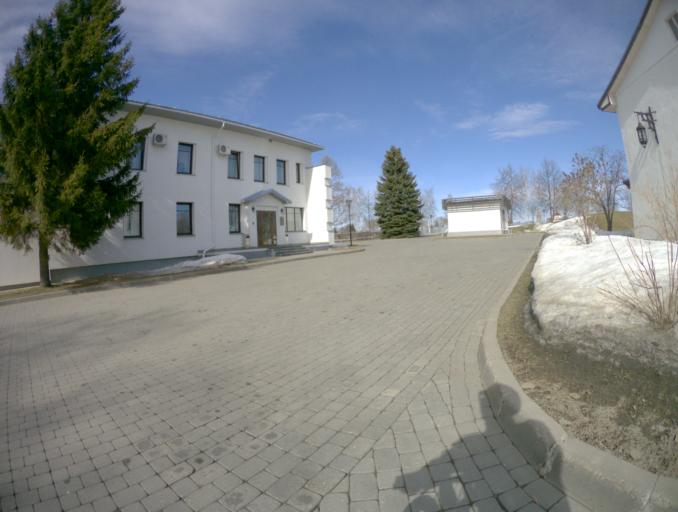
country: RU
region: Vladimir
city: Suzdal'
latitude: 56.4308
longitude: 40.4228
